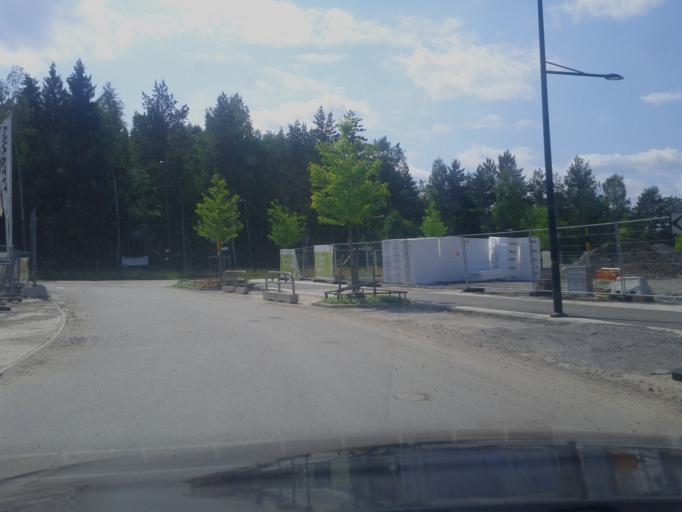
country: SE
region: Stockholm
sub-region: Taby Kommun
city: Taby
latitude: 59.4738
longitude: 18.1252
